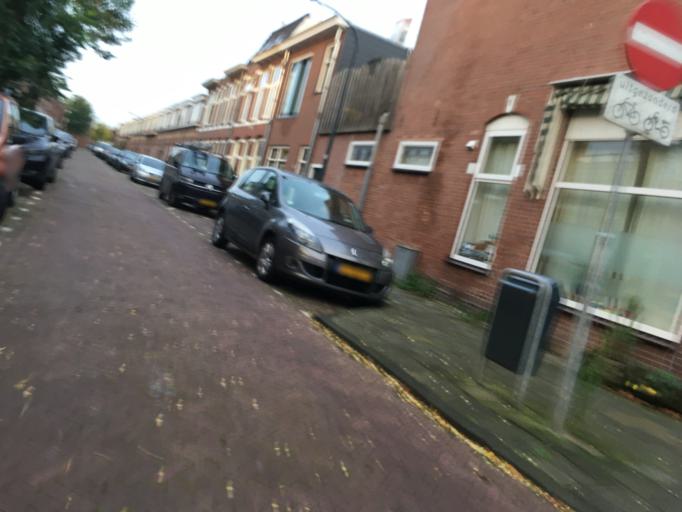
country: NL
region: North Holland
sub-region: Gemeente Haarlem
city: Haarlem
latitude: 52.3794
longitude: 4.6518
